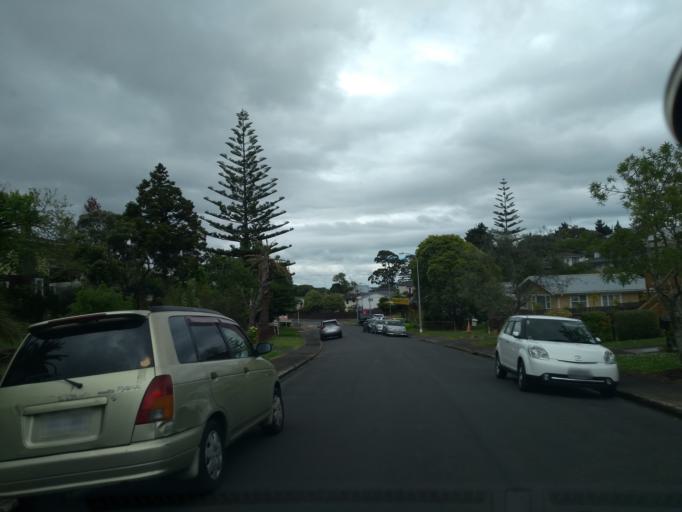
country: NZ
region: Auckland
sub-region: Auckland
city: Tamaki
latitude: -36.9119
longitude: 174.8263
